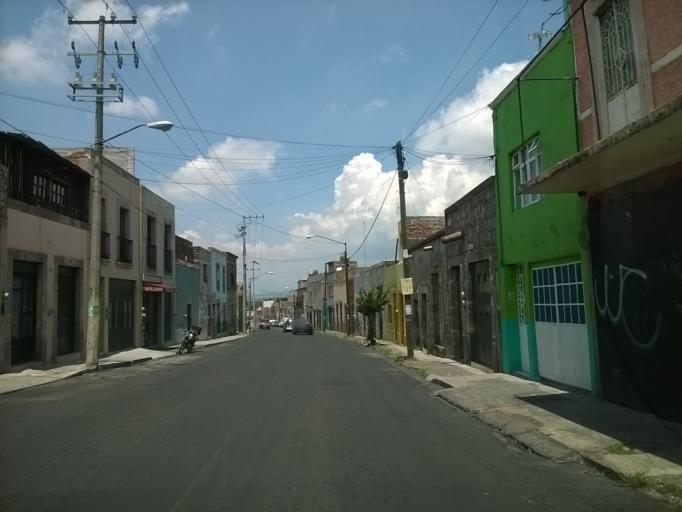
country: MX
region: Michoacan
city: Morelia
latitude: 19.7082
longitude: -101.1878
